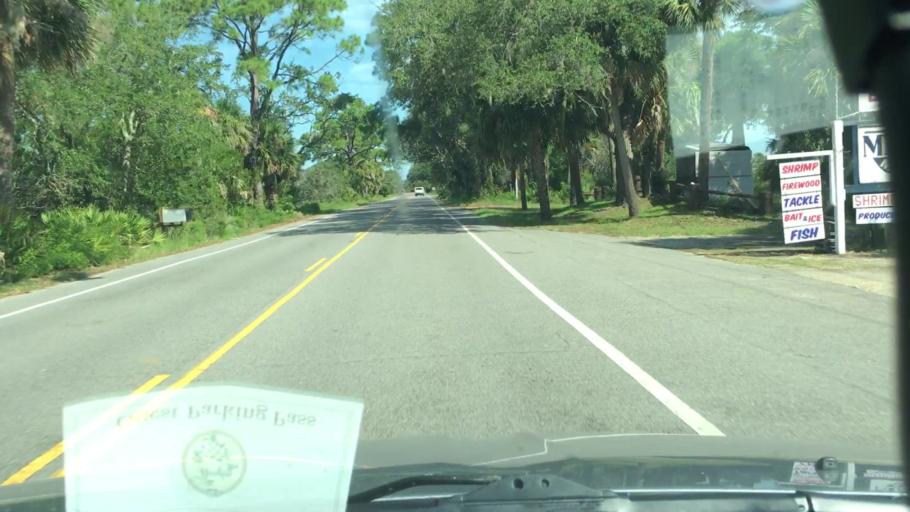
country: US
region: South Carolina
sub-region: Beaufort County
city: Beaufort
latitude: 32.3972
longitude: -80.4423
